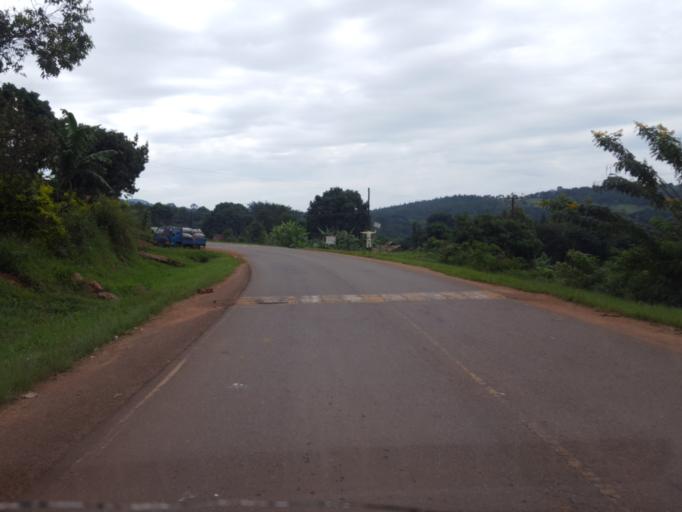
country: UG
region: Central Region
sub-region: Mityana District
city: Mityana
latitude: 0.6707
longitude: 32.0733
